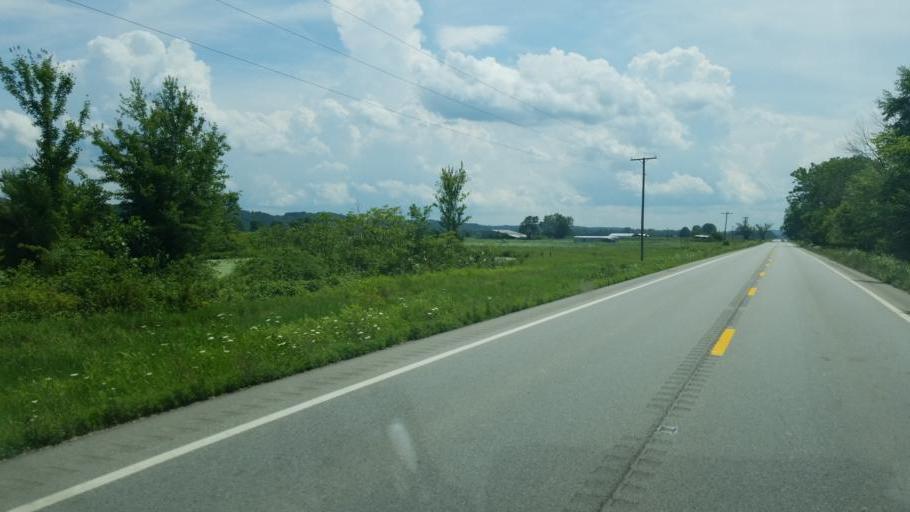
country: US
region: West Virginia
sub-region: Putnam County
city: Buffalo
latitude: 38.7093
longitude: -81.9673
